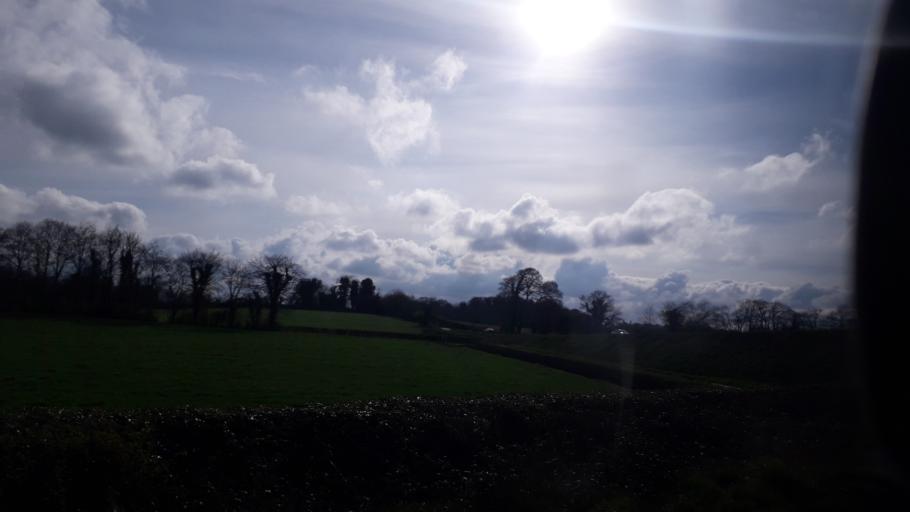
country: IE
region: Leinster
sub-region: An Mhi
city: Ballivor
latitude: 53.4732
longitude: -7.0142
